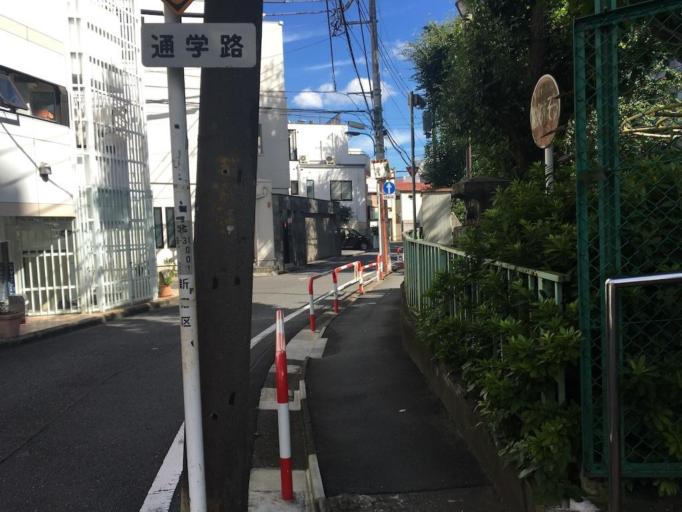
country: JP
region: Tokyo
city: Tokyo
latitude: 35.6995
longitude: 139.7100
